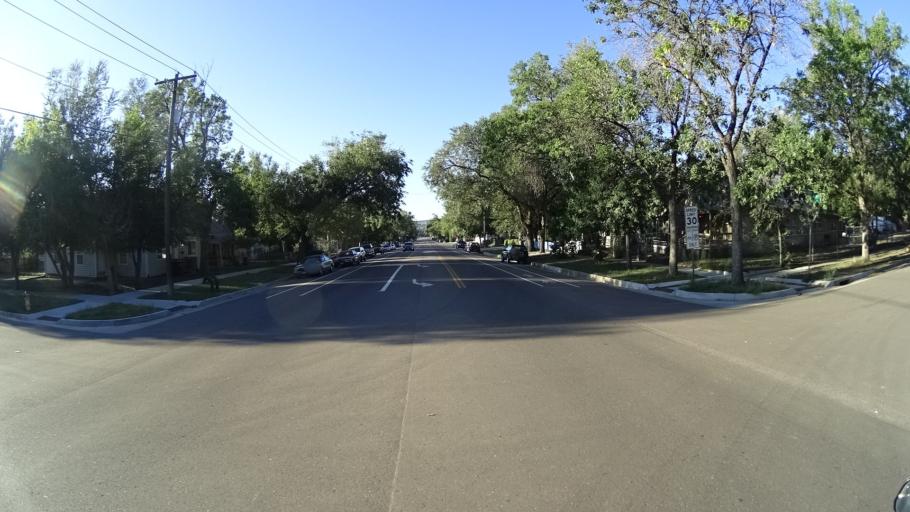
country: US
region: Colorado
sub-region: El Paso County
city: Colorado Springs
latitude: 38.8384
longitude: -104.8342
